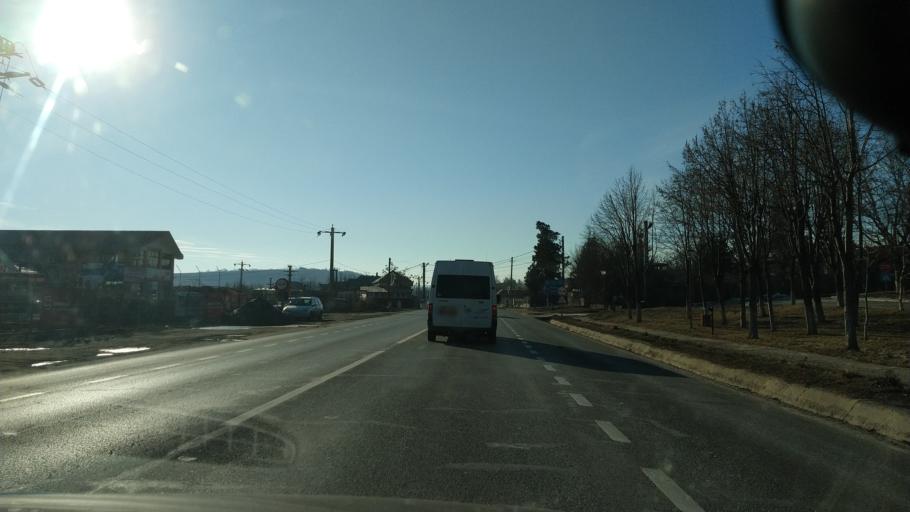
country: RO
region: Iasi
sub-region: Comuna Ion Neculce
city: Buznea
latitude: 47.2141
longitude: 27.0267
